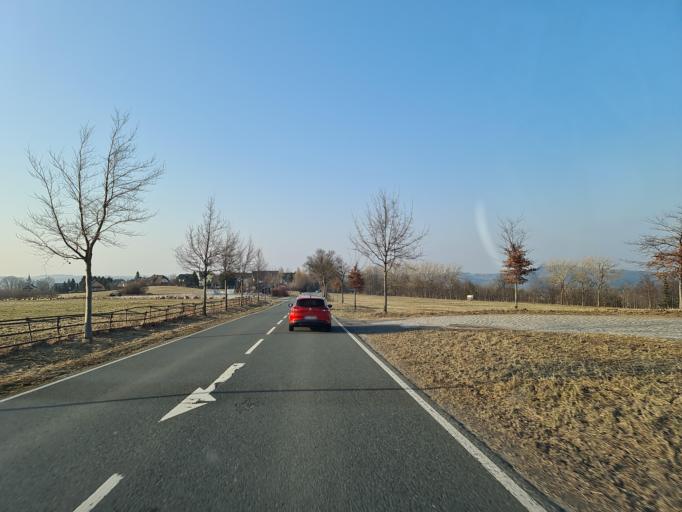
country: DE
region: Saxony
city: Eibenstock
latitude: 50.4849
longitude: 12.6089
